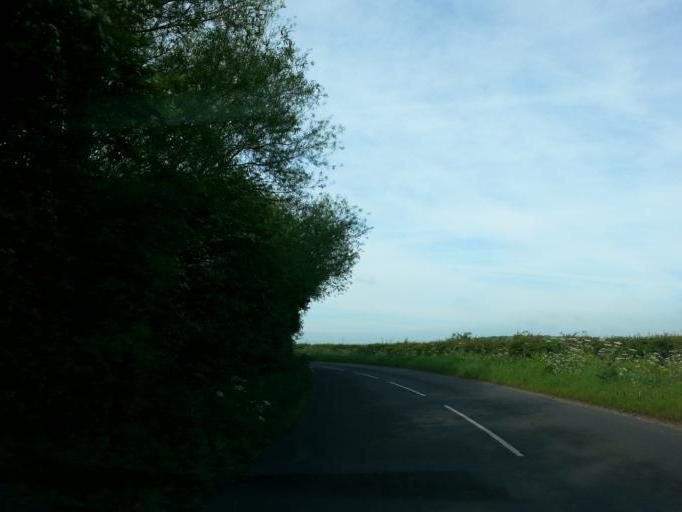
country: GB
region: England
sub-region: Nottinghamshire
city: Newark on Trent
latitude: 53.1009
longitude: -0.8329
